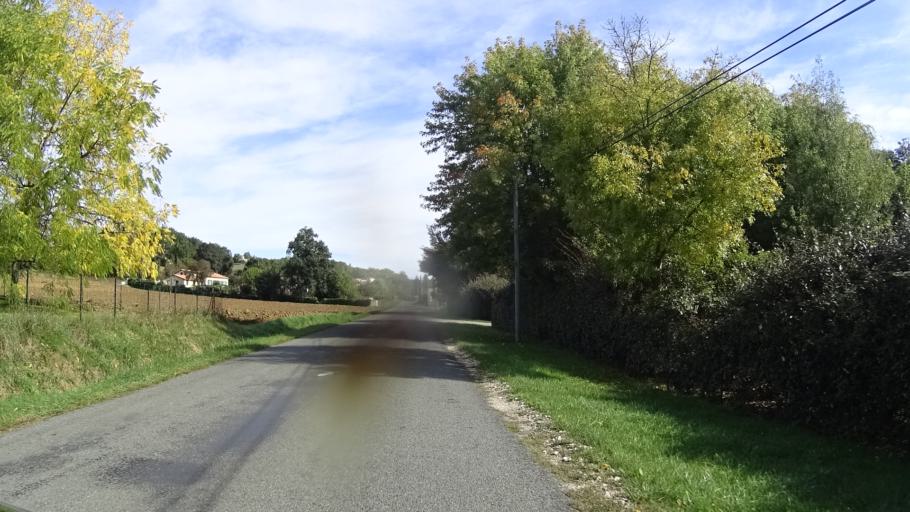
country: FR
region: Aquitaine
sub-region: Departement du Lot-et-Garonne
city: Castelculier
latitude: 44.2096
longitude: 0.7386
